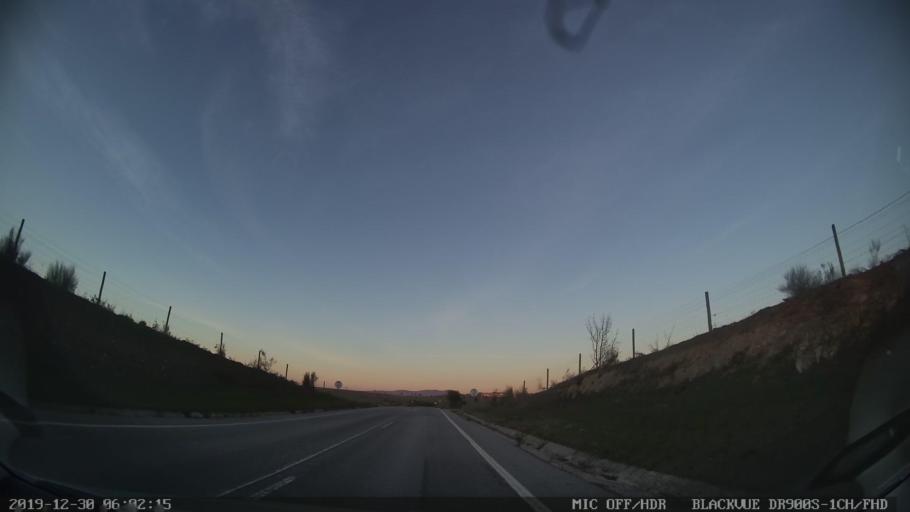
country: PT
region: Castelo Branco
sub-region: Penamacor
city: Penamacor
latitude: 40.0683
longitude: -7.2433
